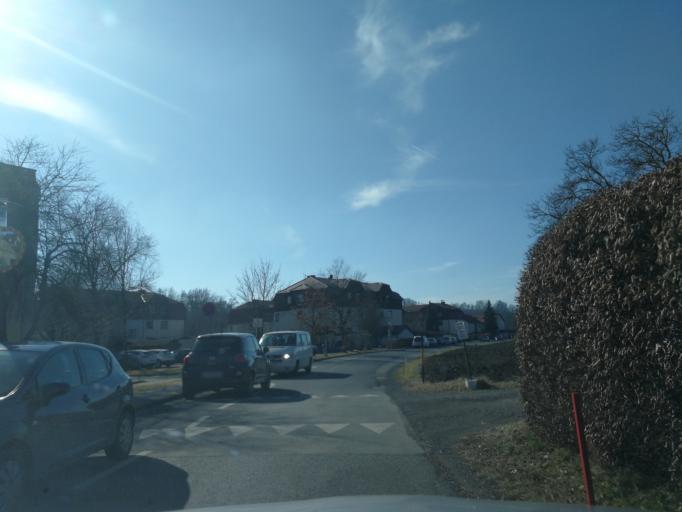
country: AT
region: Styria
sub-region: Politischer Bezirk Suedoststeiermark
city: Mureck
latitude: 46.7043
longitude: 15.7650
